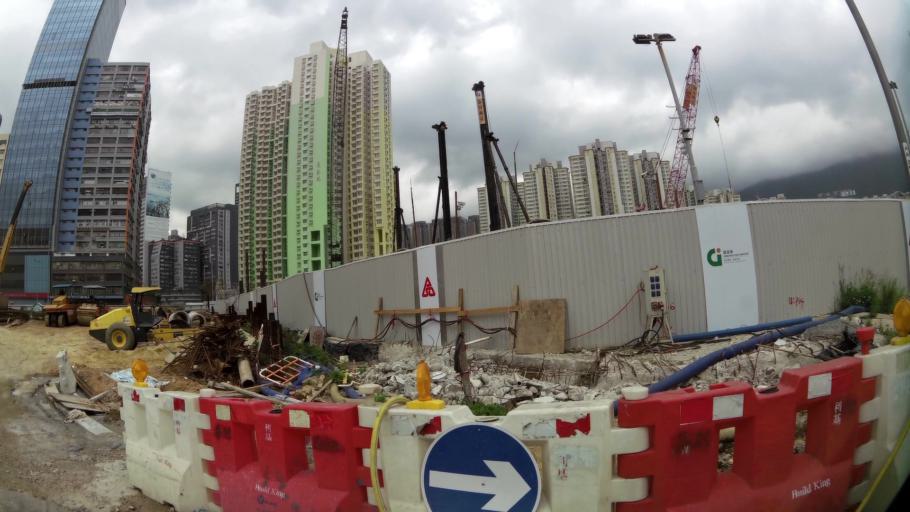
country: HK
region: Wong Tai Sin
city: Wong Tai Sin
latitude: 22.3335
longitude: 114.2004
